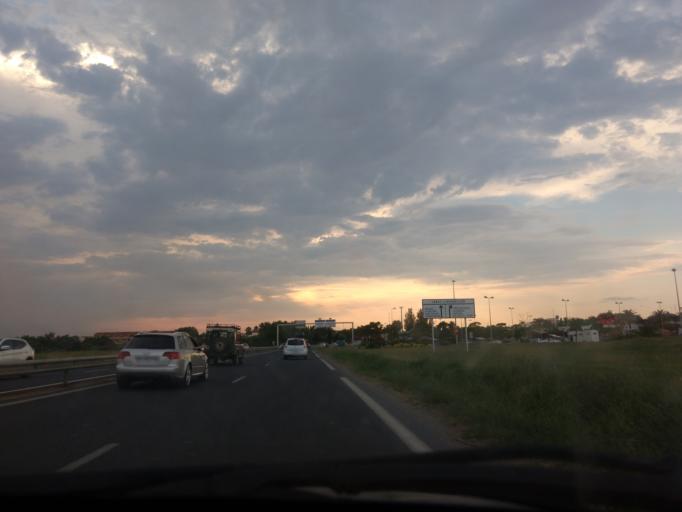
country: FR
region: Languedoc-Roussillon
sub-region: Departement des Pyrenees-Orientales
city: Canet-en-Roussillon
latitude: 42.6991
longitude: 3.0215
